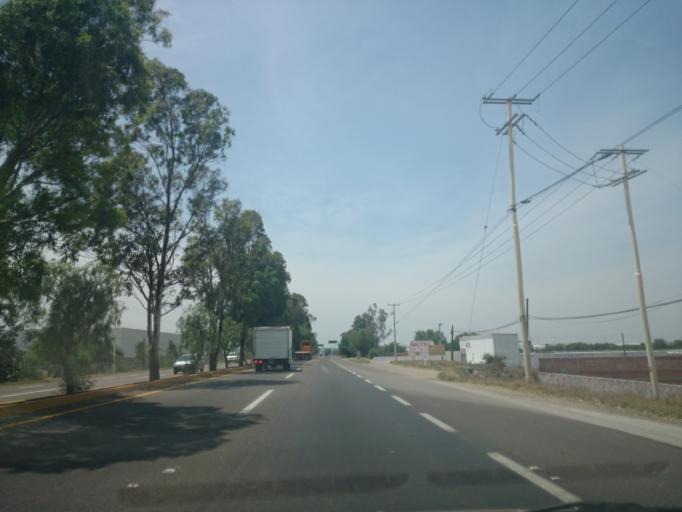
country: MX
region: Aguascalientes
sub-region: Aguascalientes
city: Penuelas (El Cienegal)
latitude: 21.7542
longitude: -102.2772
